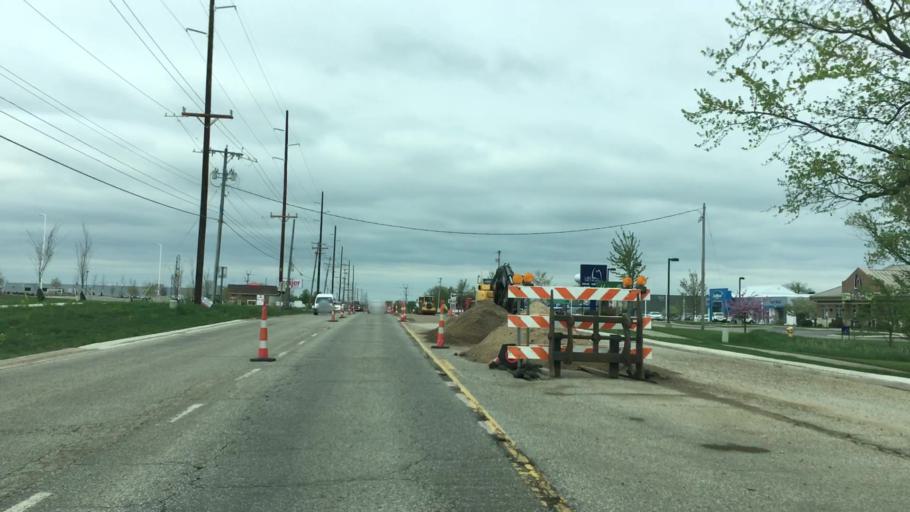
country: US
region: Michigan
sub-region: Ottawa County
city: Hudsonville
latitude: 42.8418
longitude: -85.8618
